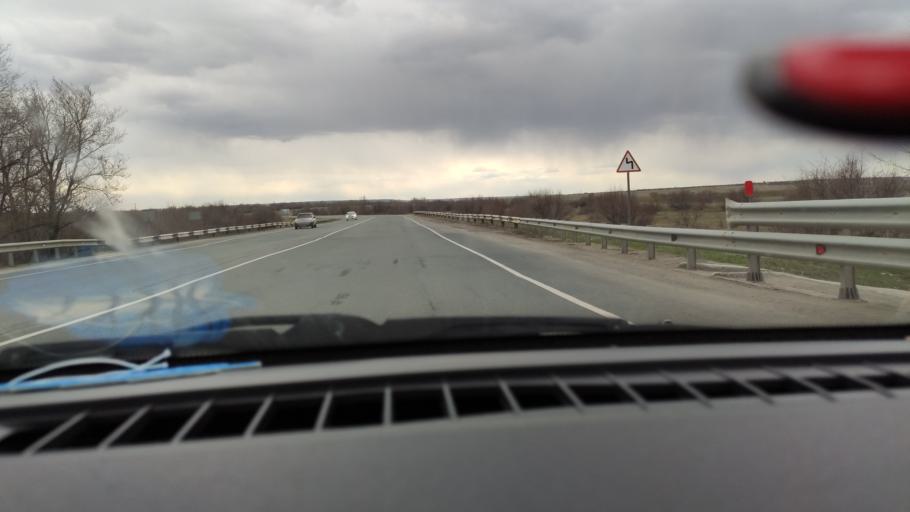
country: RU
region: Saratov
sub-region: Saratovskiy Rayon
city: Saratov
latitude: 51.7195
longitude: 46.0262
